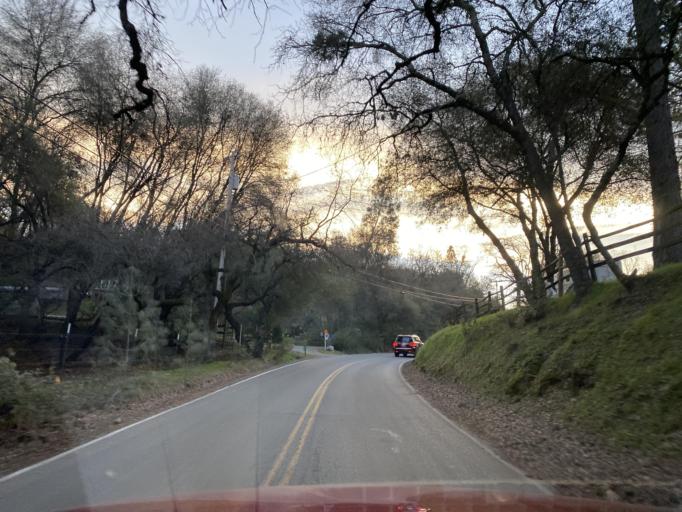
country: US
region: California
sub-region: Amador County
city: Plymouth
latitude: 38.5026
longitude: -120.7518
